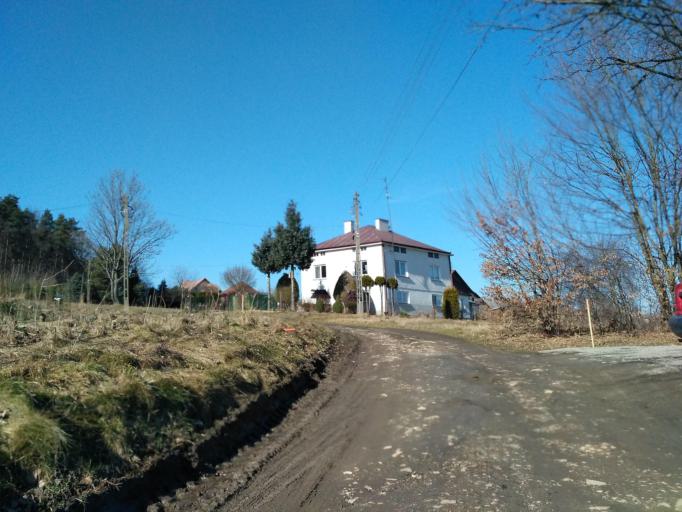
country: PL
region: Subcarpathian Voivodeship
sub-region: Powiat rzeszowski
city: Lutoryz
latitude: 49.9637
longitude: 21.8883
